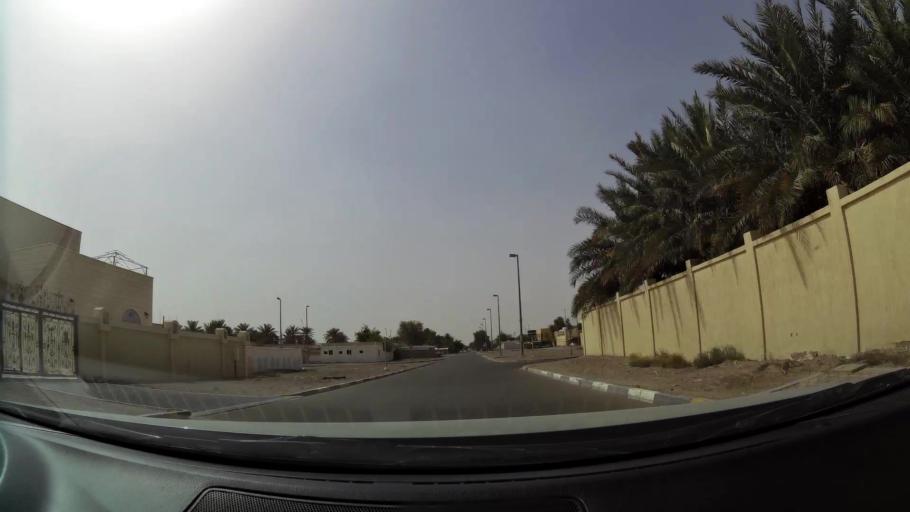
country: AE
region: Abu Dhabi
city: Al Ain
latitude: 24.1861
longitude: 55.6307
